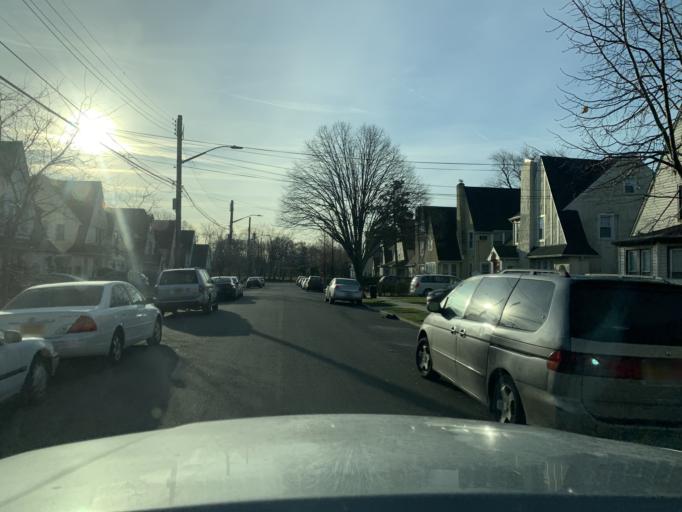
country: US
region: New York
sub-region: Queens County
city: Jamaica
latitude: 40.6923
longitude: -73.7744
